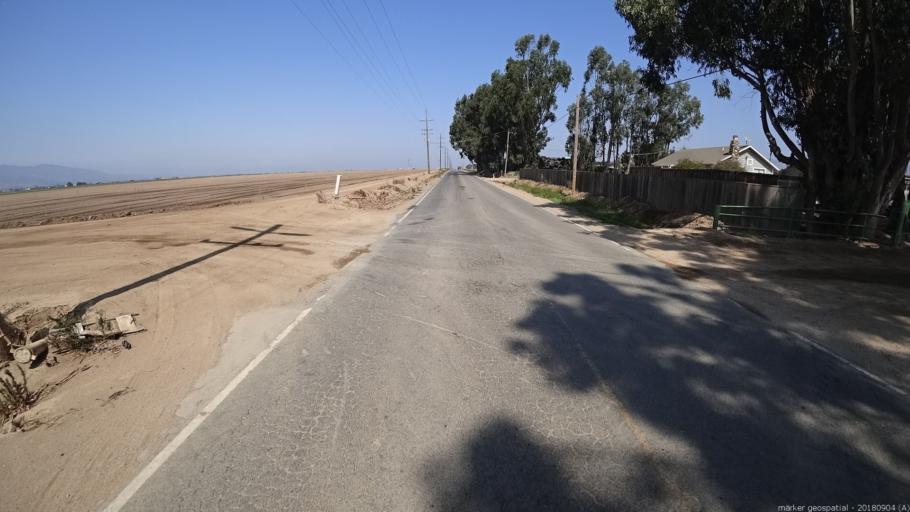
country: US
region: California
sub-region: Monterey County
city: Chualar
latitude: 36.5699
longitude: -121.4888
